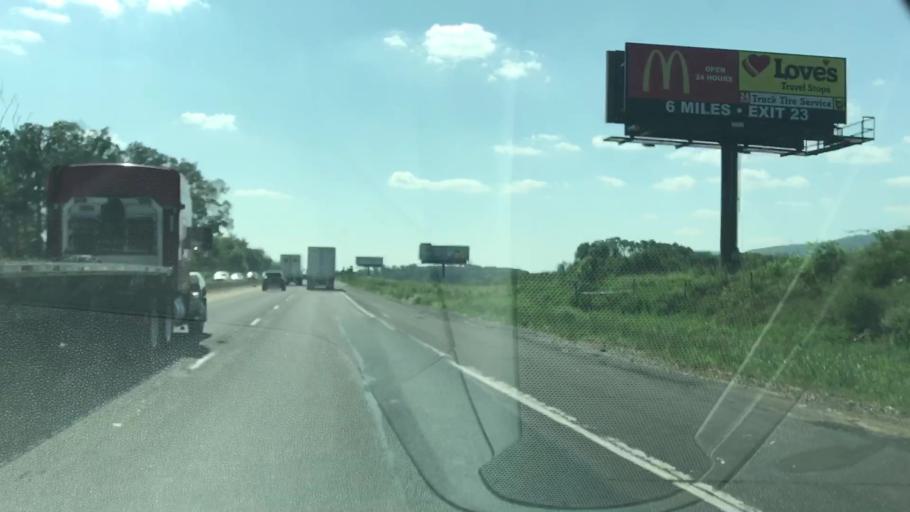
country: US
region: Pennsylvania
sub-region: Berks County
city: West Hamburg
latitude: 40.5543
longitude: -76.0072
